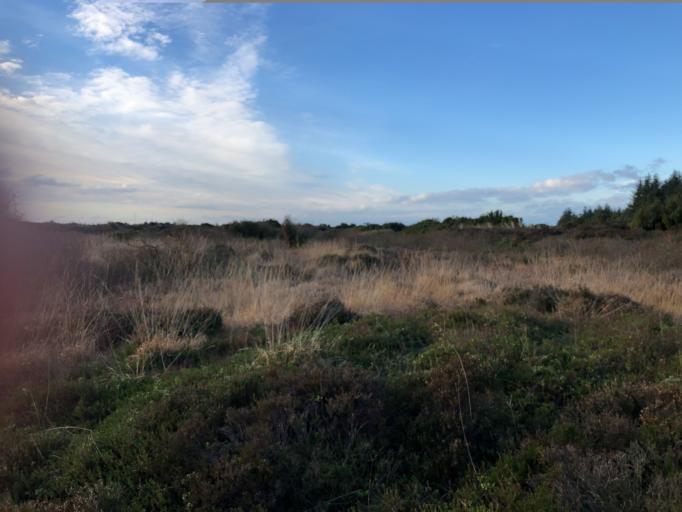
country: DK
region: Central Jutland
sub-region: Holstebro Kommune
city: Ulfborg
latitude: 56.2700
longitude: 8.3675
